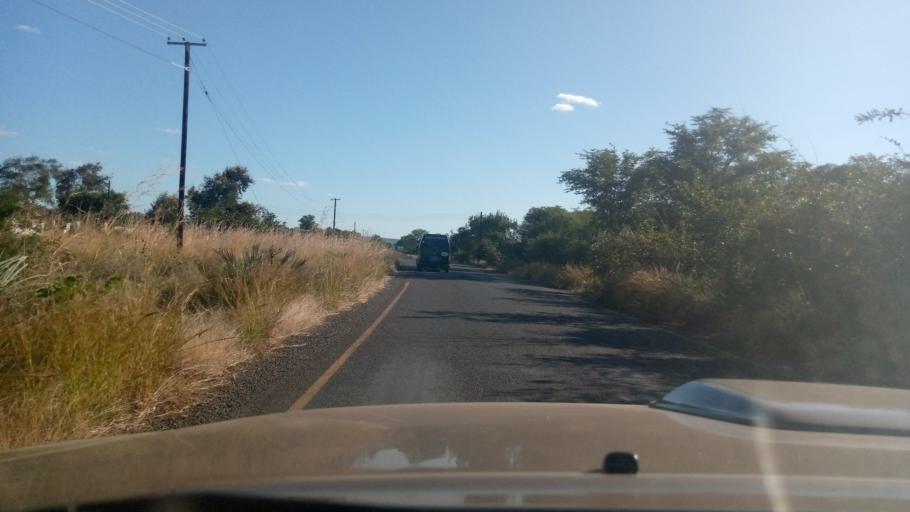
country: ZM
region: Southern
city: Livingstone
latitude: -17.8785
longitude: 25.8508
